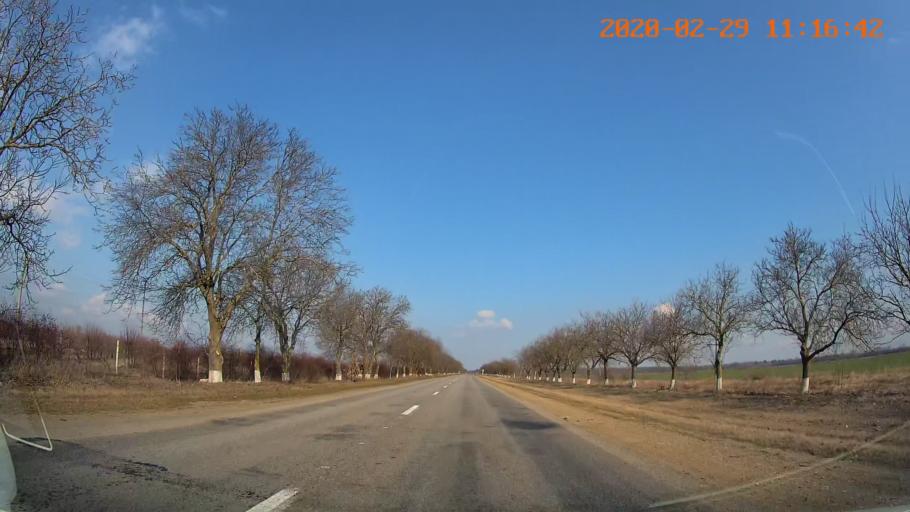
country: MD
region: Telenesti
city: Dubasari
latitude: 47.3123
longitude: 29.1685
